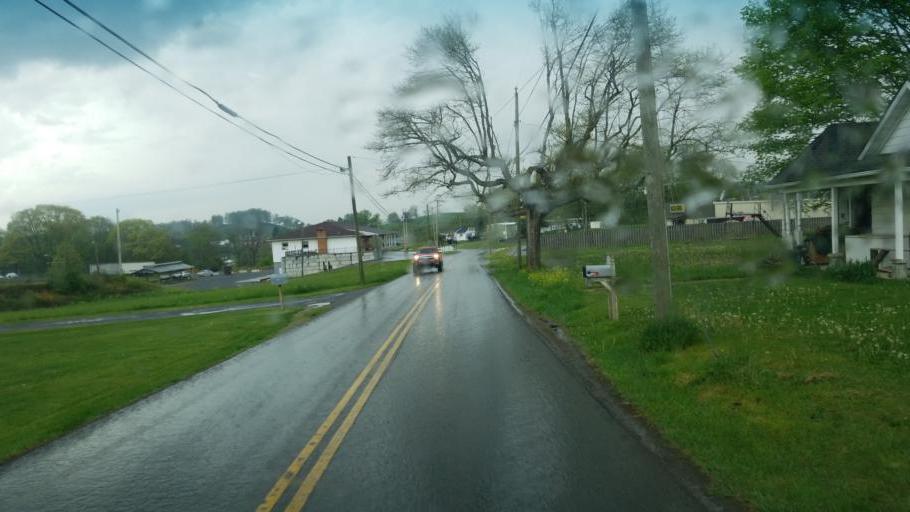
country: US
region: Virginia
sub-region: Smyth County
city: Adwolf
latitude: 36.7887
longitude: -81.5812
